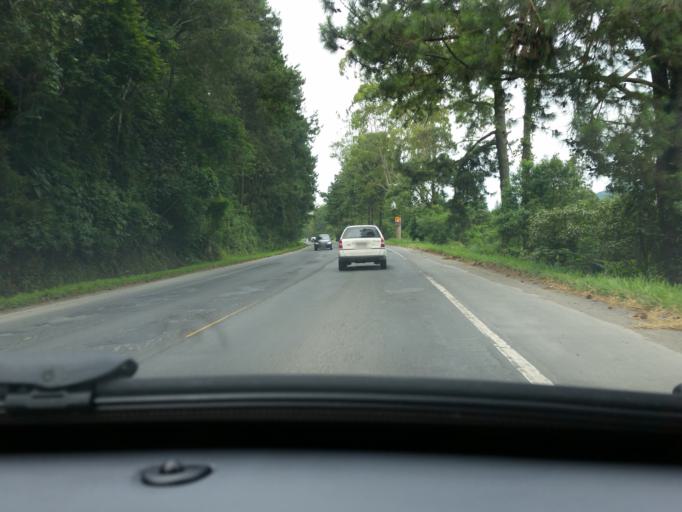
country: BR
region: Santa Catarina
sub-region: Rio Do Sul
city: Rio do Sul
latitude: -27.2540
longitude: -49.7047
